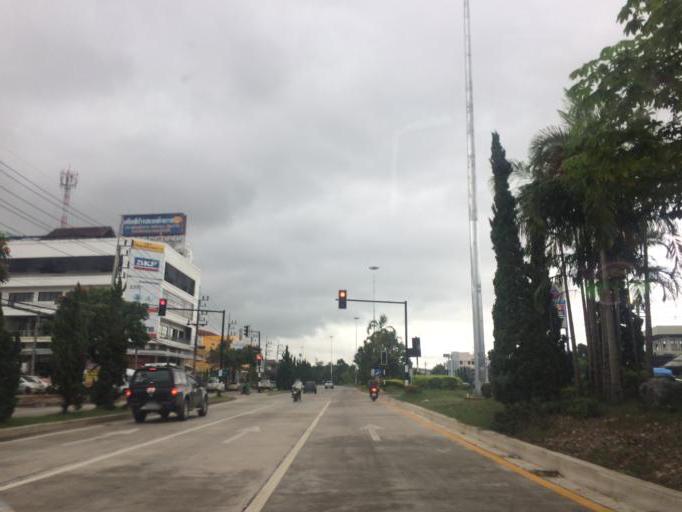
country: TH
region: Chiang Rai
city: Chiang Rai
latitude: 19.9021
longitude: 99.8401
